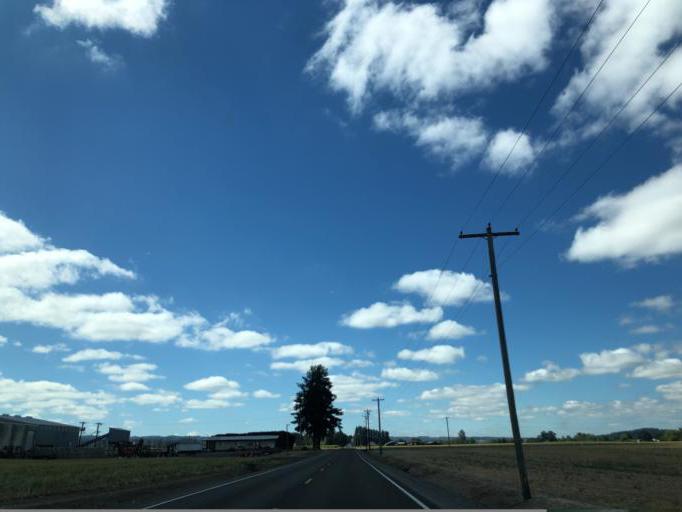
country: US
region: Oregon
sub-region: Marion County
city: Mount Angel
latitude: 45.0831
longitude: -122.7435
